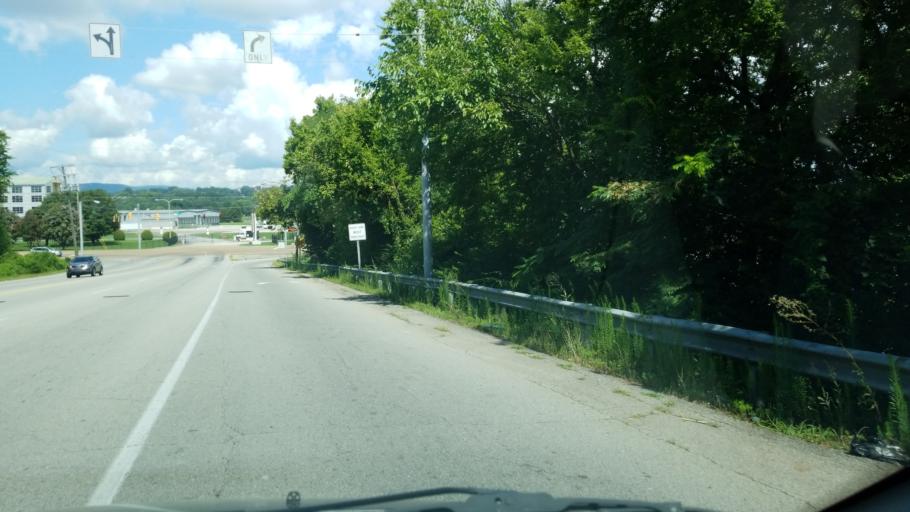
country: US
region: Tennessee
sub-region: Hamilton County
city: East Chattanooga
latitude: 35.0579
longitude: -85.2744
